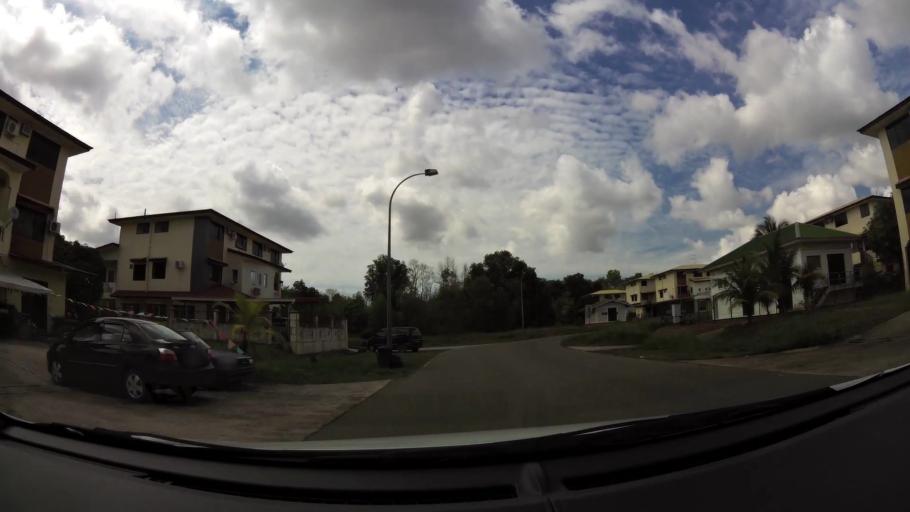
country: BN
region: Brunei and Muara
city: Bandar Seri Begawan
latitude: 4.9326
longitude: 114.8964
